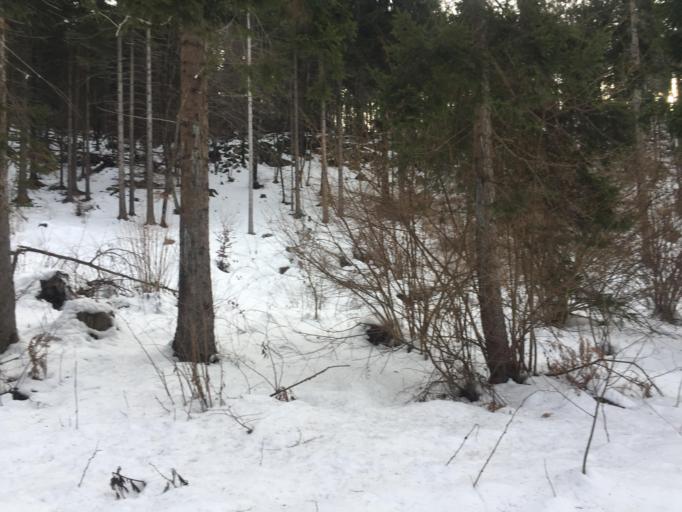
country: IT
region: Friuli Venezia Giulia
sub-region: Provincia di Udine
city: Lauco
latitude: 46.4295
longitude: 12.9487
